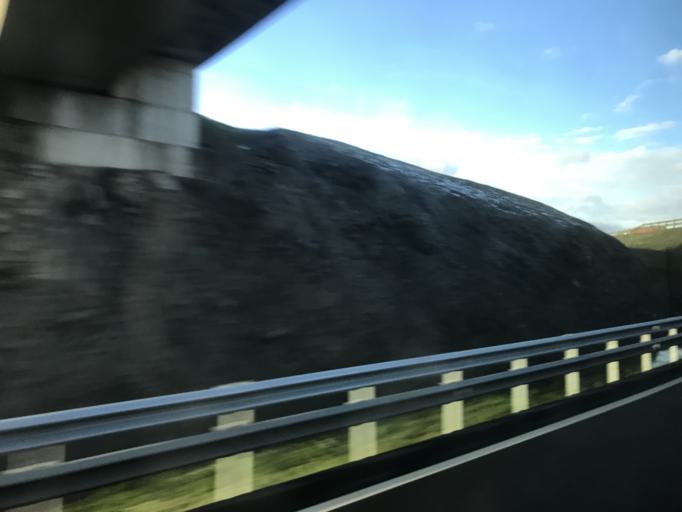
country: ES
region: Basque Country
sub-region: Provincia de Alava
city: Gasteiz / Vitoria
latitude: 42.8258
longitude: -2.7638
